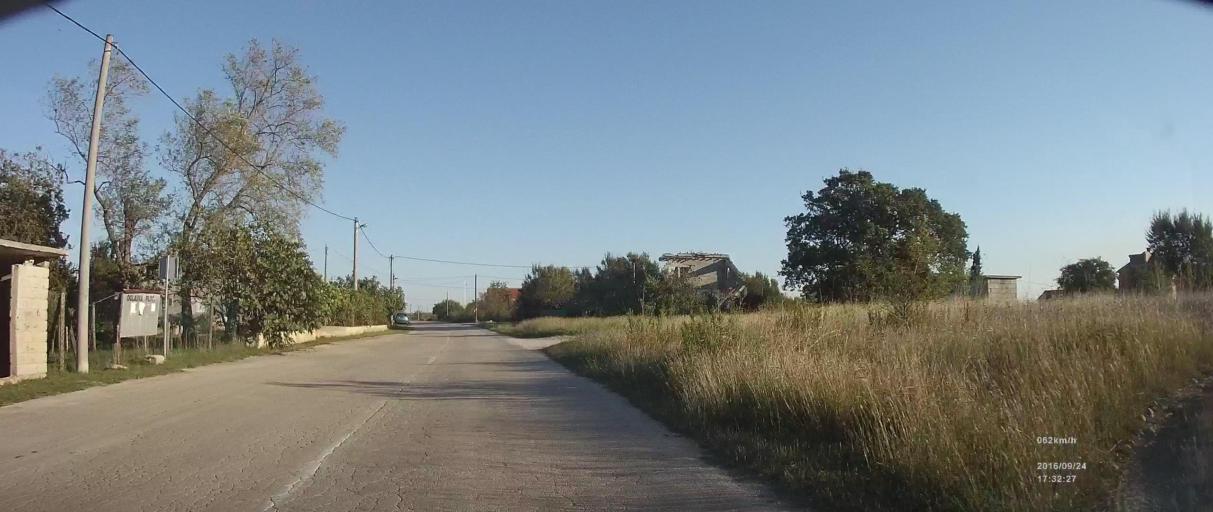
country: HR
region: Zadarska
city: Posedarje
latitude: 44.1822
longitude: 15.4503
